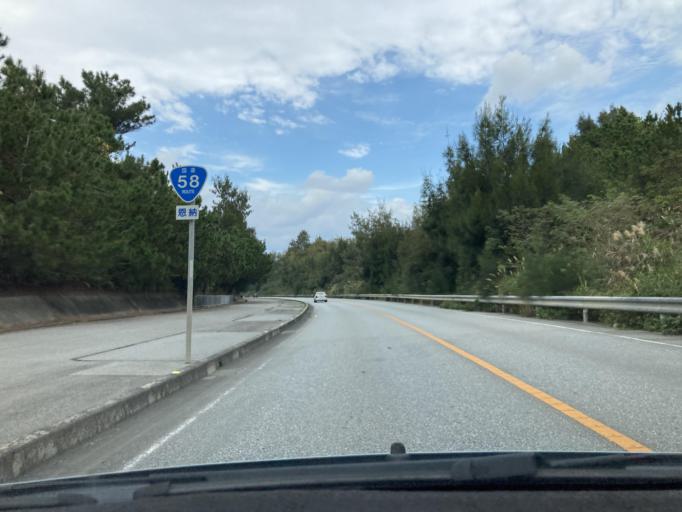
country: JP
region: Okinawa
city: Ishikawa
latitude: 26.4856
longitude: 127.8536
